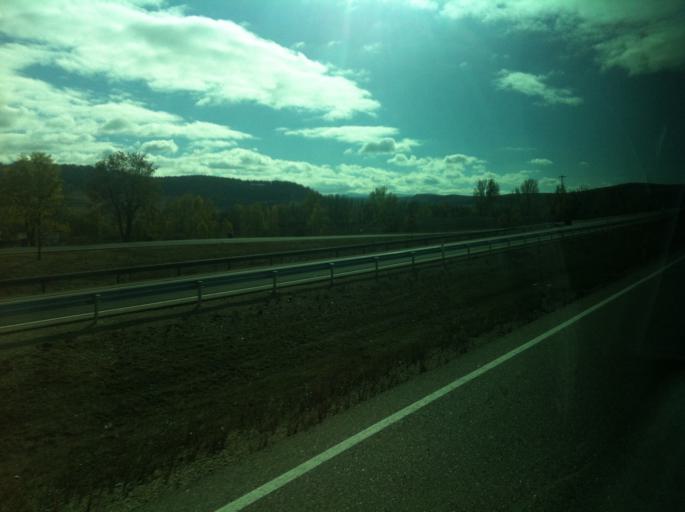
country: ES
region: Castille and Leon
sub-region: Provincia de Burgos
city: Santa Olalla de Bureba
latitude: 42.4666
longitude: -3.4487
